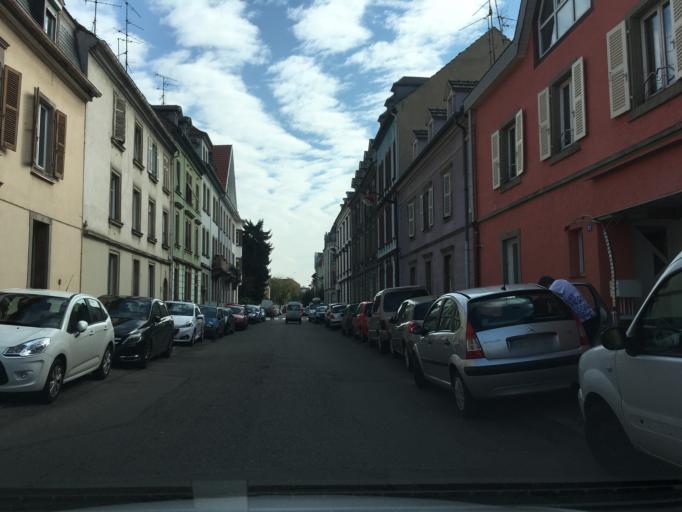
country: FR
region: Alsace
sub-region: Departement du Haut-Rhin
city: Colmar
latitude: 48.0803
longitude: 7.3455
